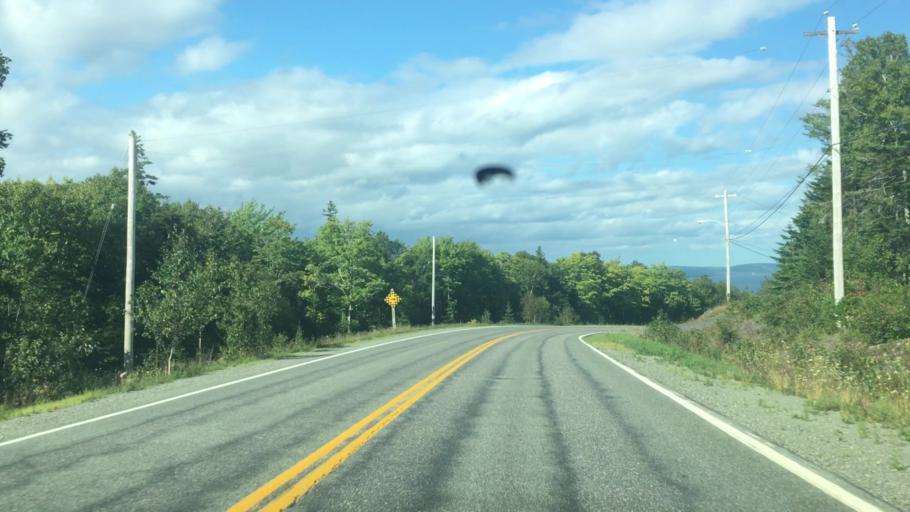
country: CA
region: Nova Scotia
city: Sydney
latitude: 45.8631
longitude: -60.6253
